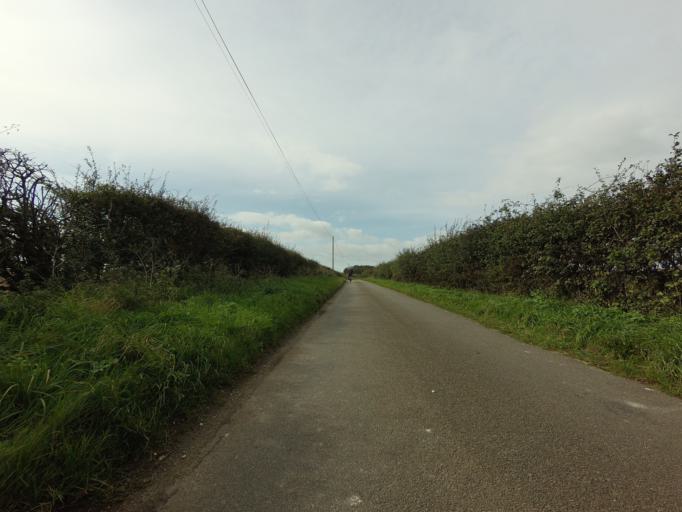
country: GB
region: England
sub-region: Norfolk
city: Wells-next-the-Sea
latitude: 52.9397
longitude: 0.6978
